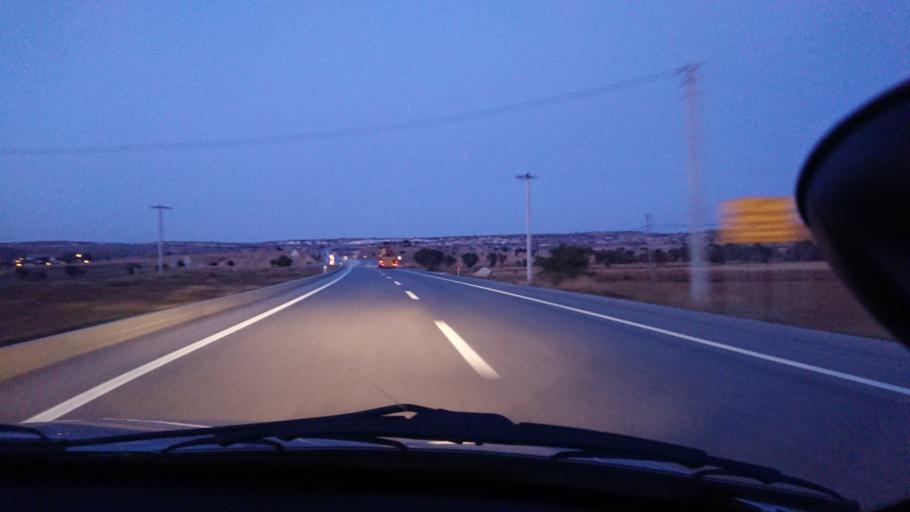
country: TR
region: Kuetahya
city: Cavdarhisar
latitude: 39.1273
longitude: 29.5443
